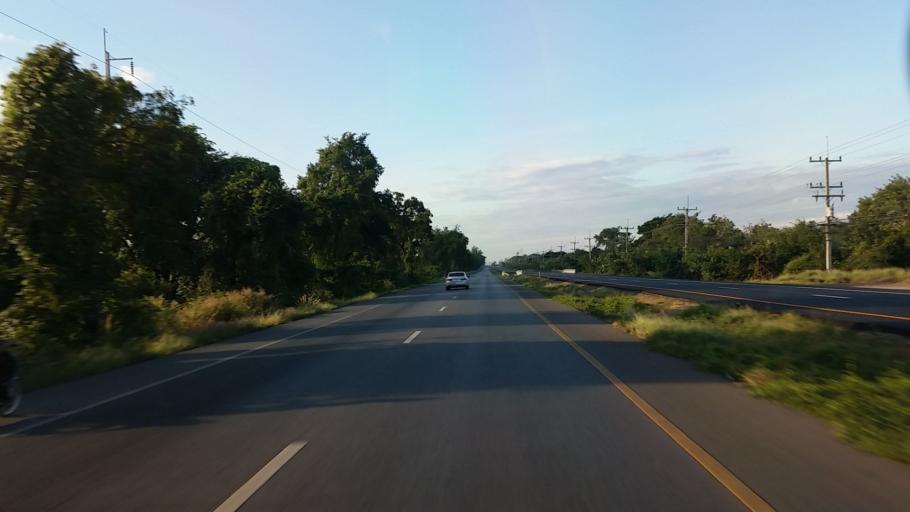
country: TH
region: Lop Buri
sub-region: Amphoe Tha Luang
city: Tha Luang
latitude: 15.1040
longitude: 101.0220
